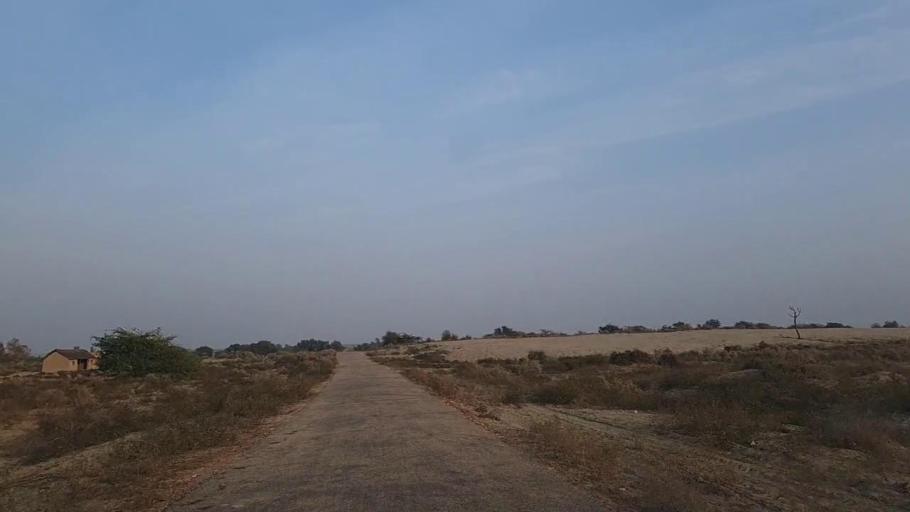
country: PK
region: Sindh
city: Jam Sahib
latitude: 26.4074
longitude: 68.5962
